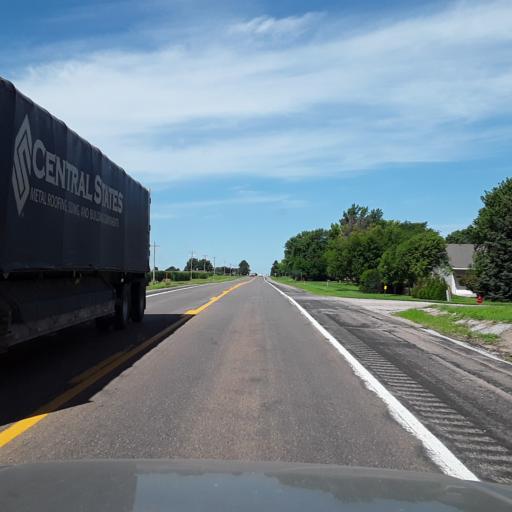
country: US
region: Nebraska
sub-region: Seward County
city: Seward
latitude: 40.9016
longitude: -97.1449
